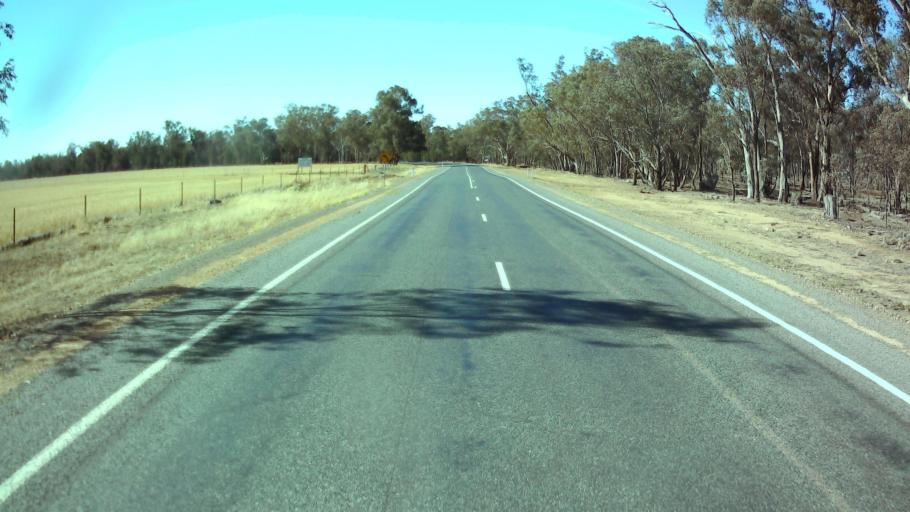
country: AU
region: New South Wales
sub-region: Weddin
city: Grenfell
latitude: -33.7318
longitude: 148.0888
